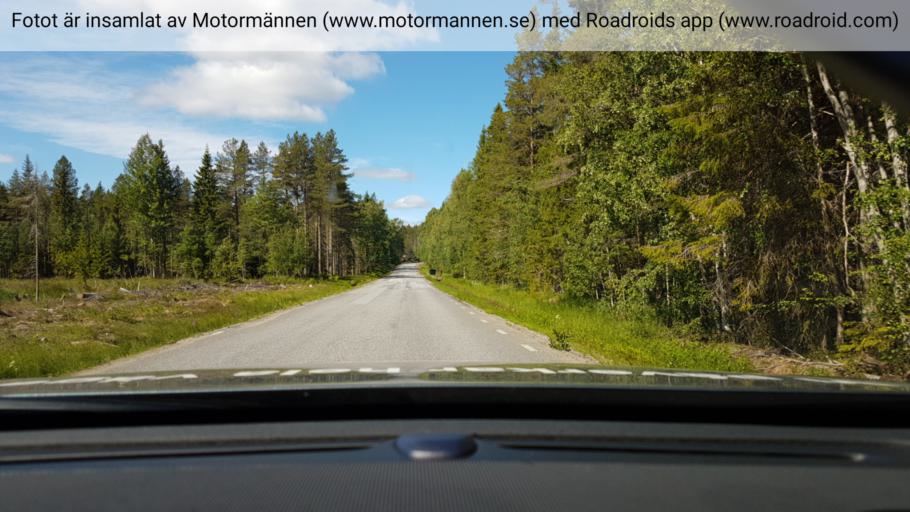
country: SE
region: Vaesterbotten
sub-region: Skelleftea Kommun
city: Burea
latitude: 64.4468
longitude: 21.4736
